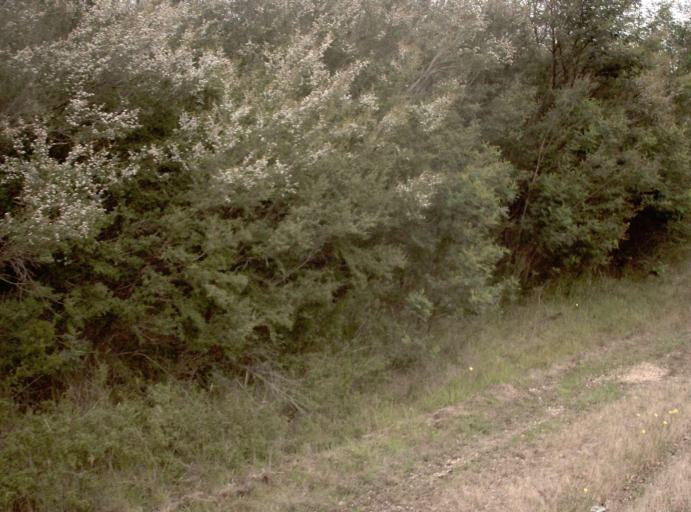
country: AU
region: Victoria
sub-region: East Gippsland
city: Bairnsdale
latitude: -37.7079
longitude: 147.3157
